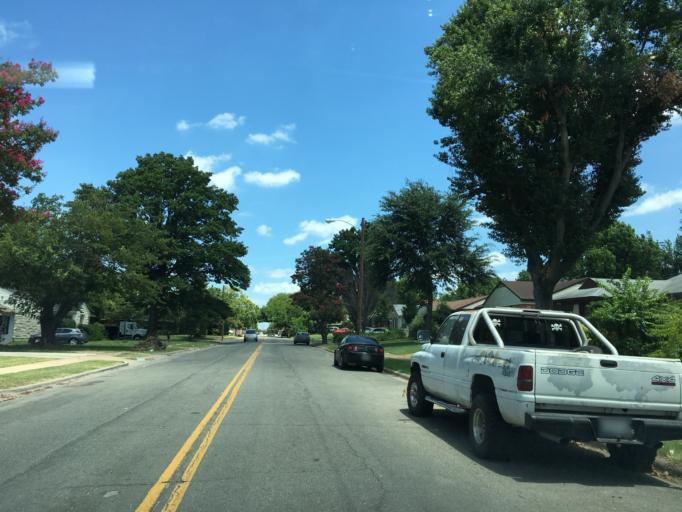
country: US
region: Texas
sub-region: Dallas County
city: Garland
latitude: 32.8480
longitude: -96.6729
